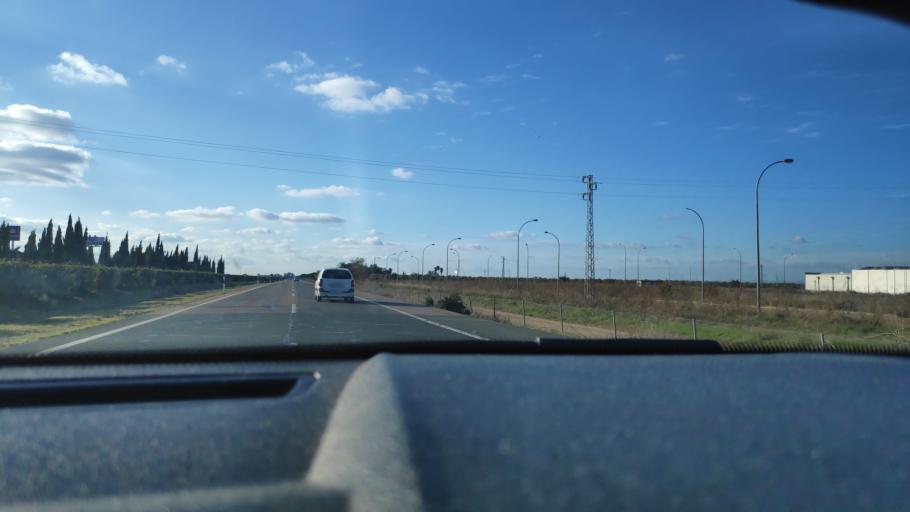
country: ES
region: Andalusia
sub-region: Provincia de Sevilla
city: La Luisiana
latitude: 37.5238
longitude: -5.2046
